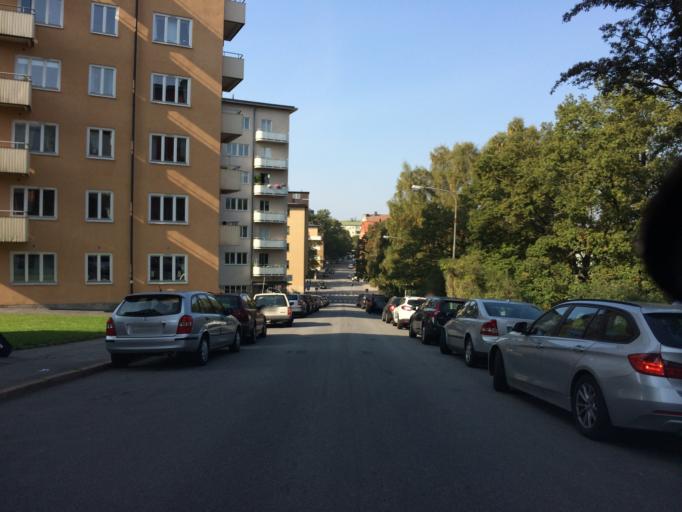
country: SE
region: Stockholm
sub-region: Solna Kommun
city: Solna
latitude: 59.3291
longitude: 18.0045
